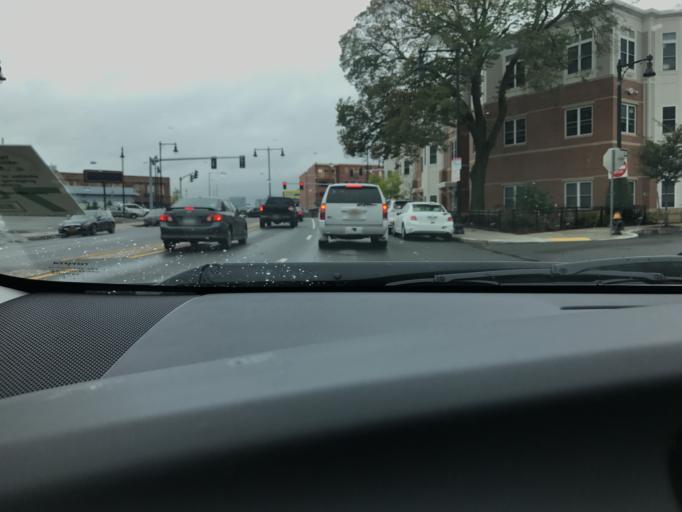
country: US
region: Massachusetts
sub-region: Suffolk County
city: South Boston
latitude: 42.3309
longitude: -71.0527
